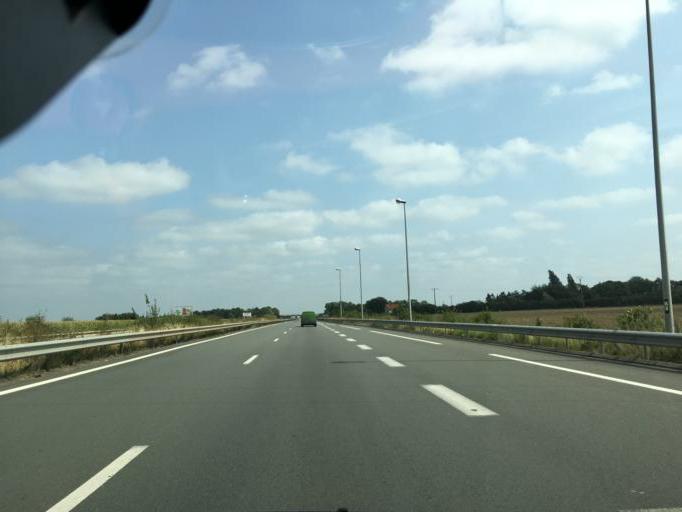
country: FR
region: Nord-Pas-de-Calais
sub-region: Departement du Nord
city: Somain
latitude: 50.3459
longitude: 3.2862
